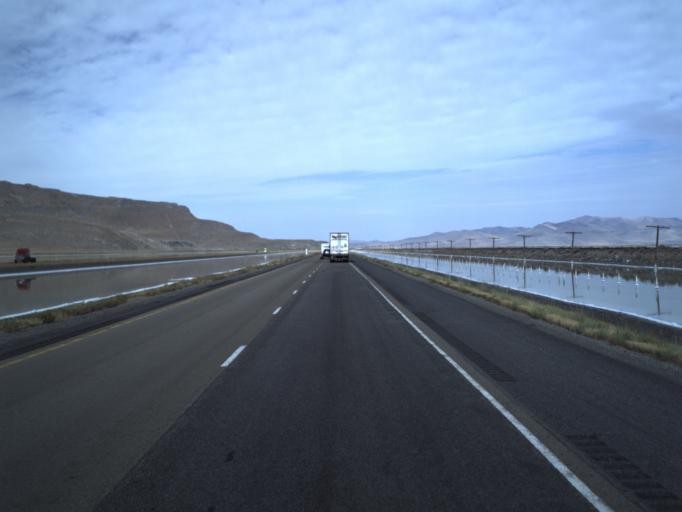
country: US
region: Utah
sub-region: Tooele County
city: Grantsville
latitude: 40.7312
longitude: -112.5914
